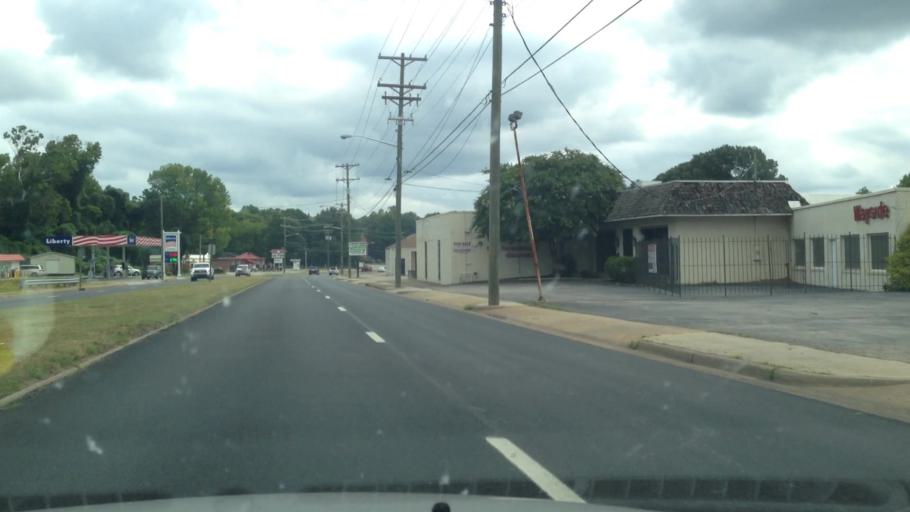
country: US
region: Virginia
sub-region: City of Danville
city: Danville
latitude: 36.5618
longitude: -79.4516
